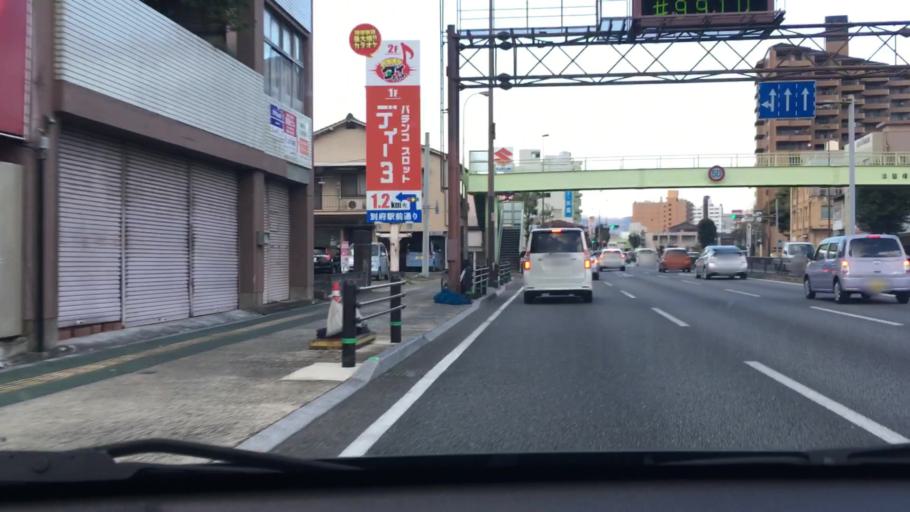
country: JP
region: Oita
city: Beppu
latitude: 33.2689
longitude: 131.5103
